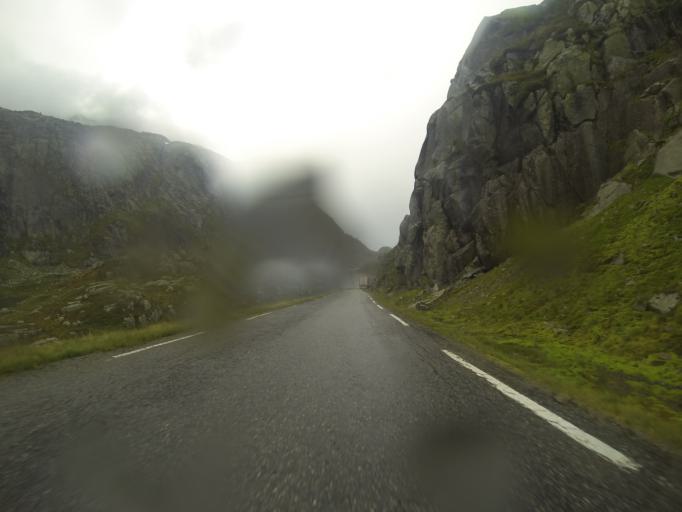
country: NO
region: Hordaland
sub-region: Odda
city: Odda
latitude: 59.7663
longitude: 6.7323
